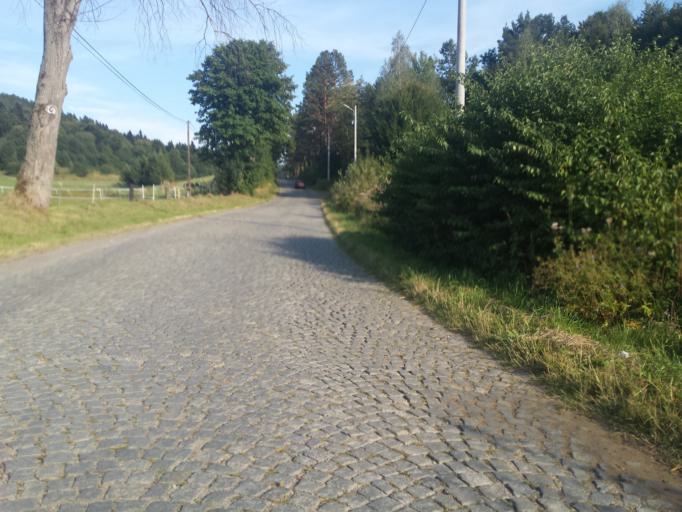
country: PL
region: Subcarpathian Voivodeship
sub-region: Powiat leski
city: Uherce Mineralne
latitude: 49.4444
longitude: 22.4024
